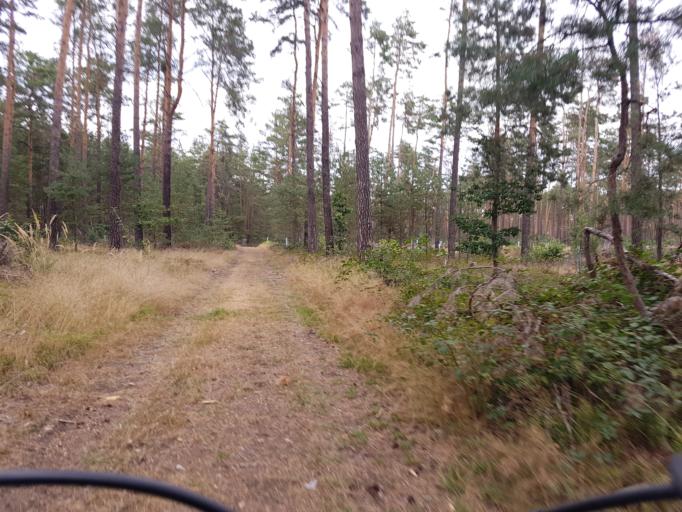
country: DE
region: Brandenburg
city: Trobitz
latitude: 51.5609
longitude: 13.4476
